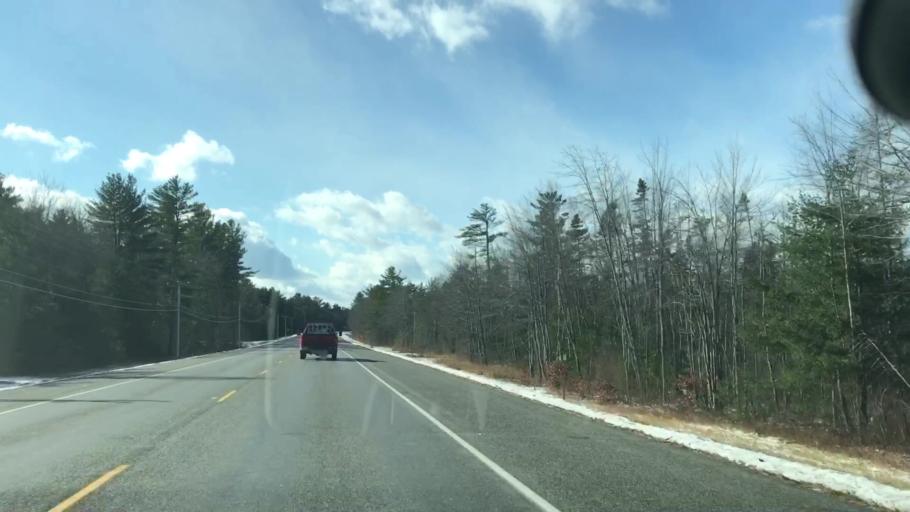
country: US
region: New Hampshire
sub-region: Carroll County
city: Ossipee
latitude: 43.7695
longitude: -71.1182
